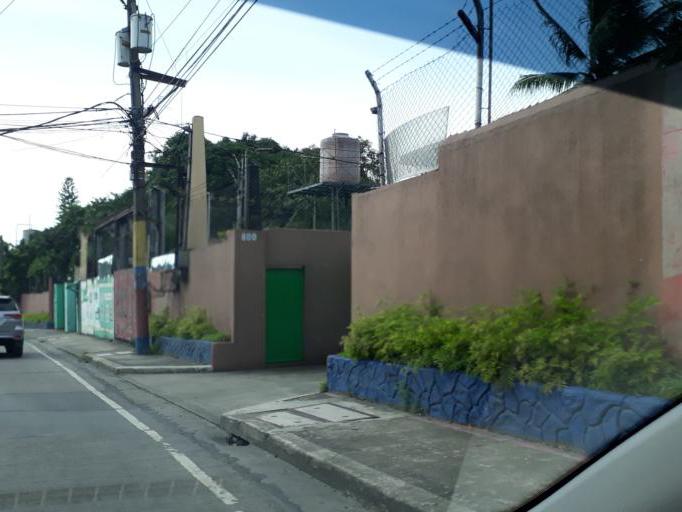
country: PH
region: Metro Manila
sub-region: Caloocan City
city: Niugan
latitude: 14.6700
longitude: 120.9750
